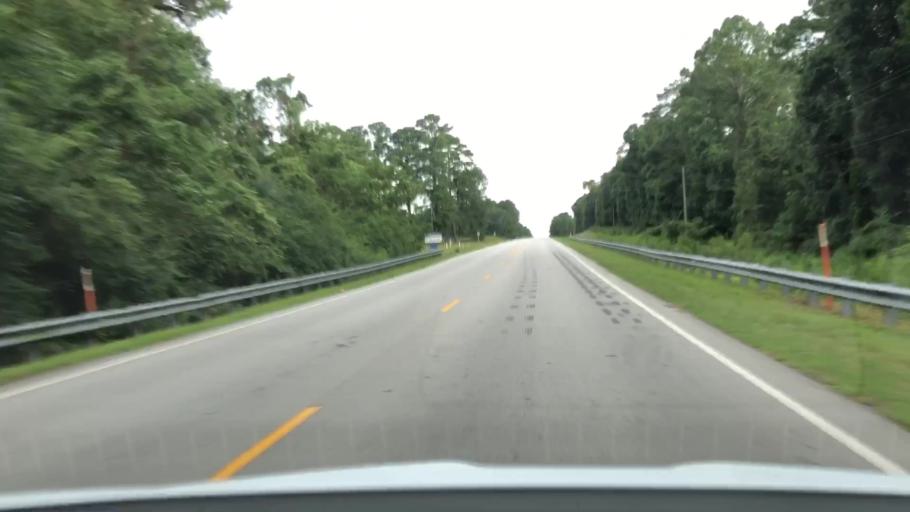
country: US
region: North Carolina
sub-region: Jones County
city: Trenton
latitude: 35.0064
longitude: -77.2815
